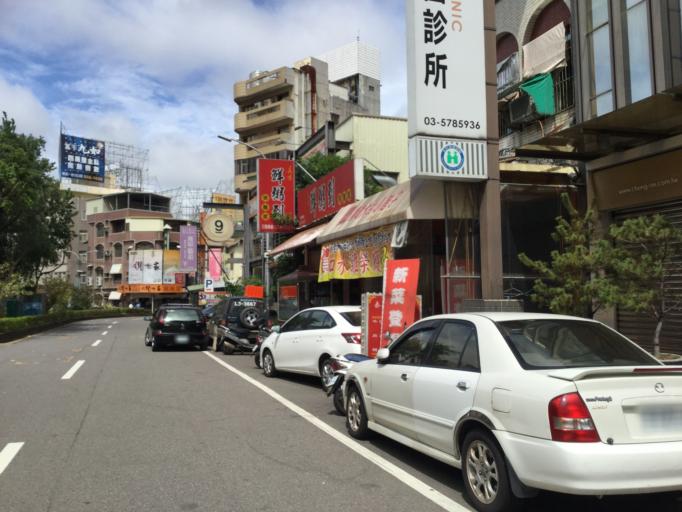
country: TW
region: Taiwan
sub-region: Hsinchu
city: Hsinchu
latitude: 24.7860
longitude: 121.0102
